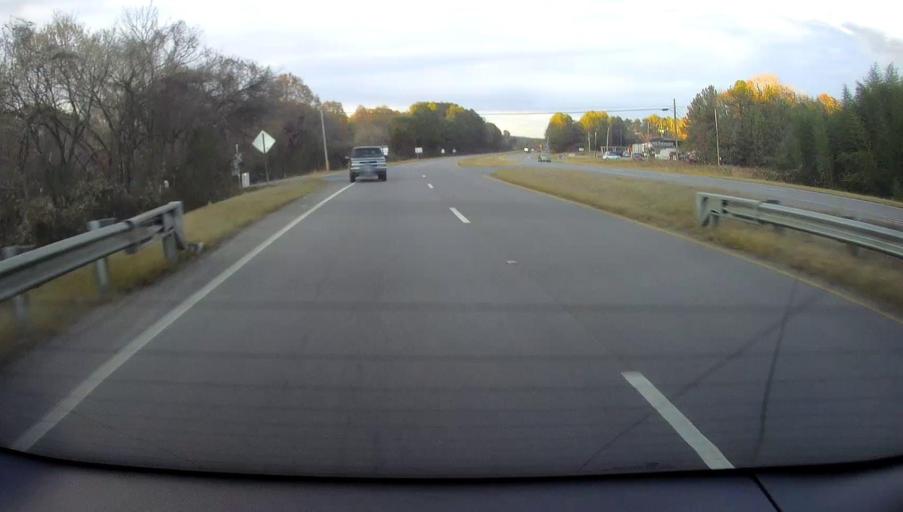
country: US
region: Alabama
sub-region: Etowah County
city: Attalla
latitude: 34.0363
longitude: -86.1117
